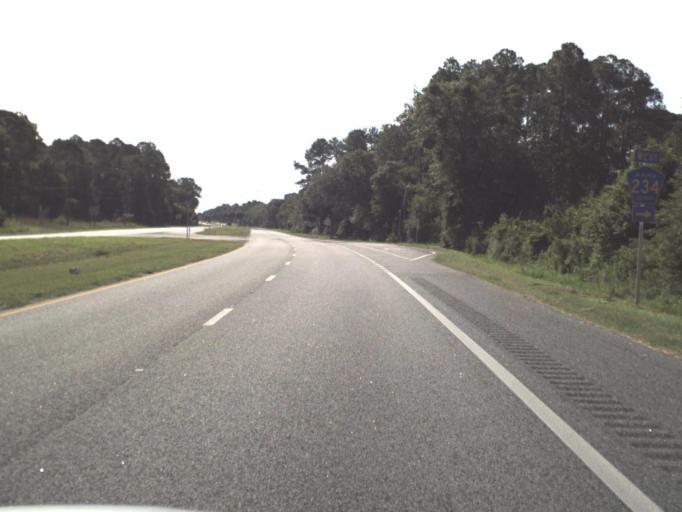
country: US
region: Florida
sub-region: Alachua County
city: Gainesville
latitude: 29.5142
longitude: -82.2913
